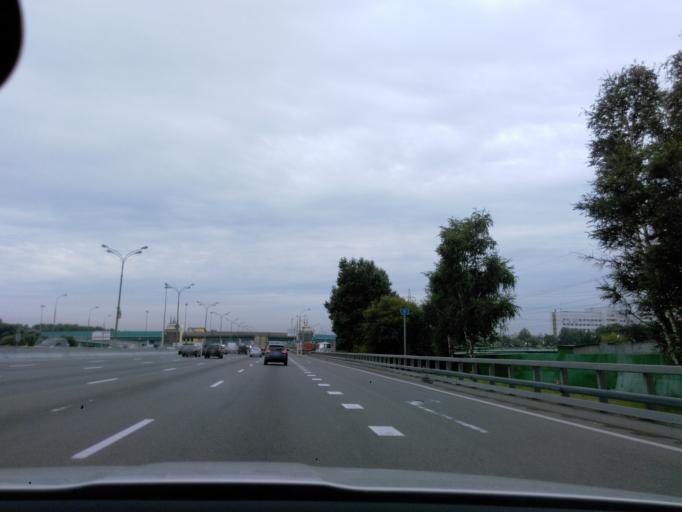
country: RU
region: Moskovskaya
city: Kuskovo
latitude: 55.7352
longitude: 37.8409
